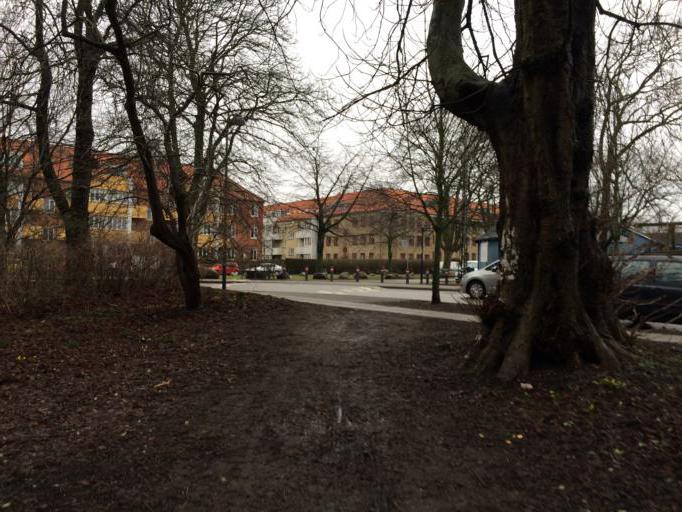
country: DK
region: Capital Region
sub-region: Frederiksberg Kommune
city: Frederiksberg
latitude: 55.6466
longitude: 12.5307
